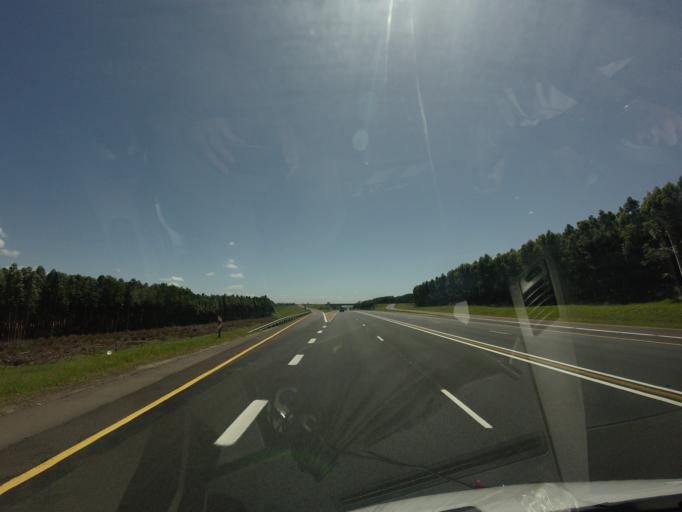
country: ZA
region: KwaZulu-Natal
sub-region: uThungulu District Municipality
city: eSikhawini
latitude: -28.9956
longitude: 31.6963
